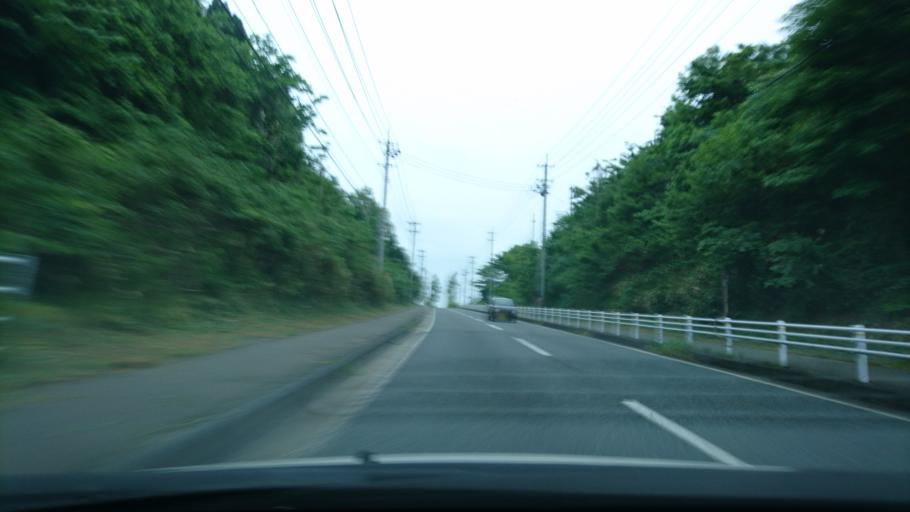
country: JP
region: Iwate
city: Ichinoseki
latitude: 38.9206
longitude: 141.1509
